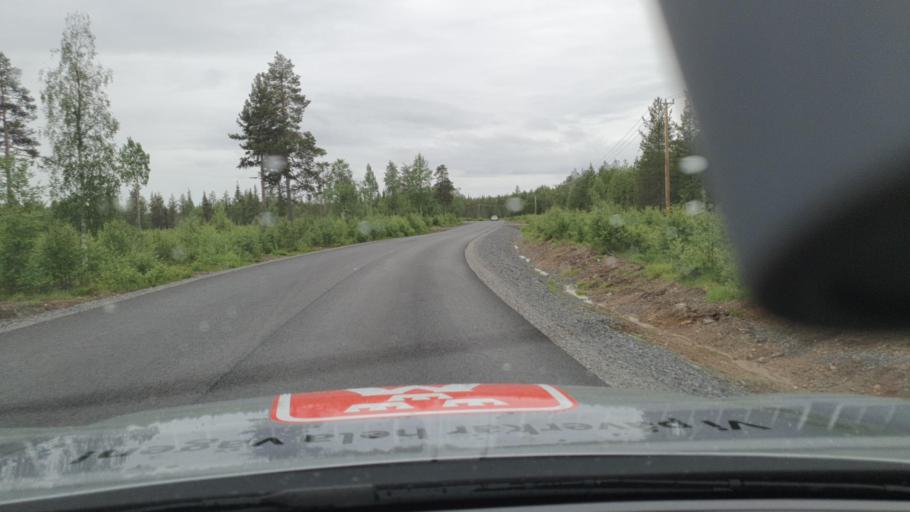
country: SE
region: Norrbotten
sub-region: Overkalix Kommun
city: OEverkalix
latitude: 66.7049
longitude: 23.2068
